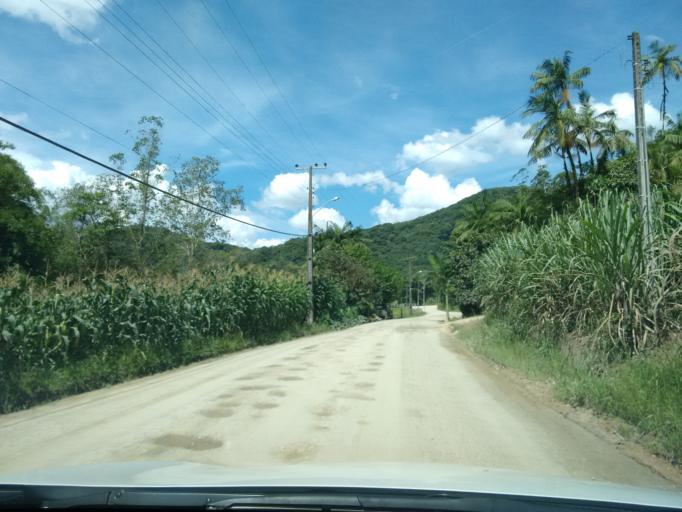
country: BR
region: Santa Catarina
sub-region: Pomerode
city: Pomerode
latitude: -26.6939
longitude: -49.1137
